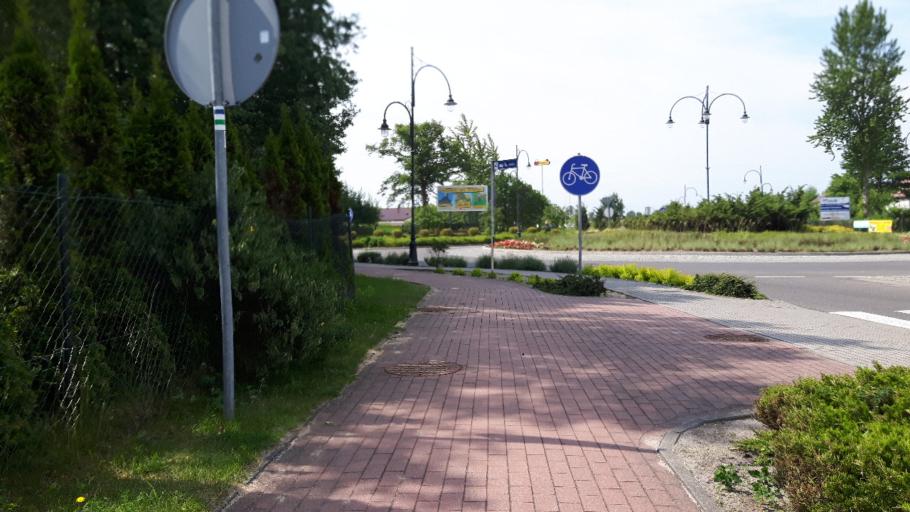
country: PL
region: Pomeranian Voivodeship
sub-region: Powiat leborski
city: Leba
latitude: 54.7512
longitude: 17.5624
